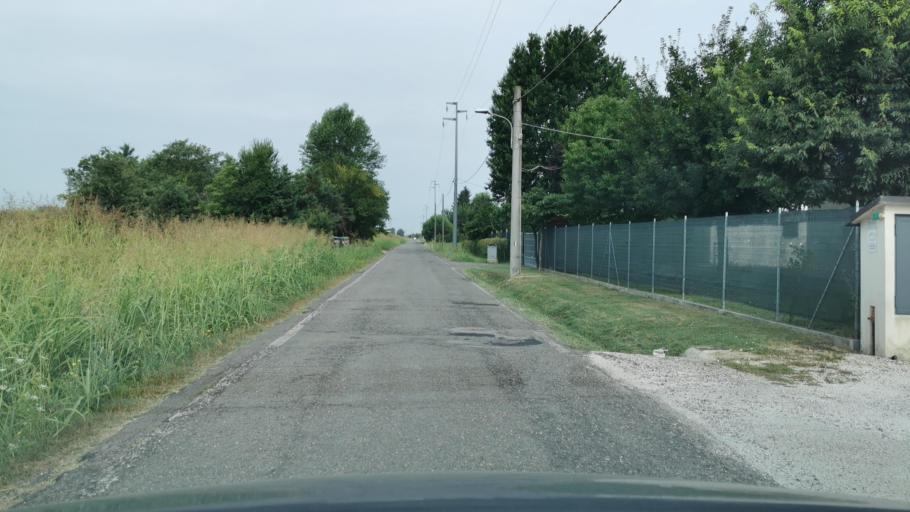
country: IT
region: Emilia-Romagna
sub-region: Provincia di Modena
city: Villanova
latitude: 44.6863
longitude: 10.9060
